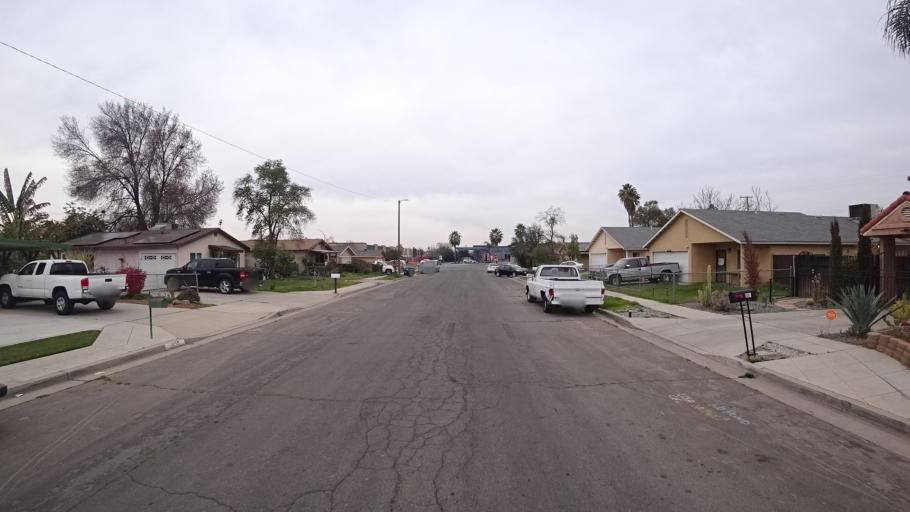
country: US
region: California
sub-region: Fresno County
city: Fresno
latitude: 36.8409
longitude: -119.8009
